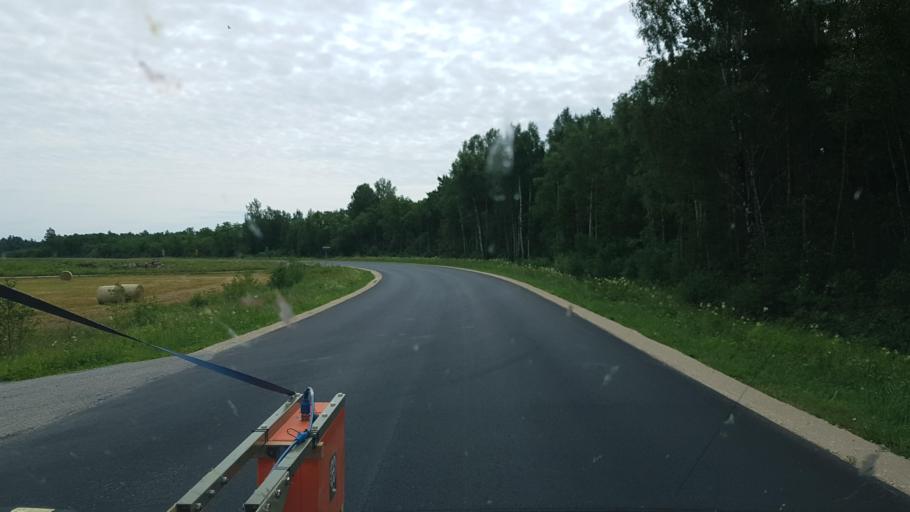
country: EE
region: Paernumaa
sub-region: Halinga vald
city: Parnu-Jaagupi
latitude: 58.6203
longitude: 24.2734
